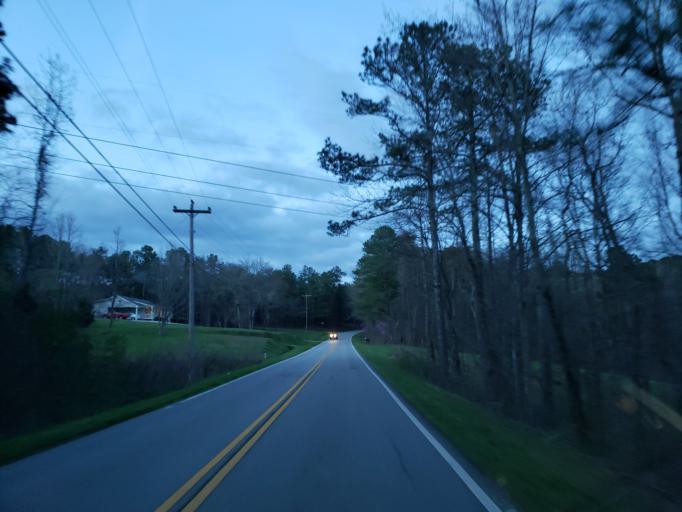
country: US
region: Georgia
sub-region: Paulding County
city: Dallas
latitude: 34.0137
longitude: -84.8749
